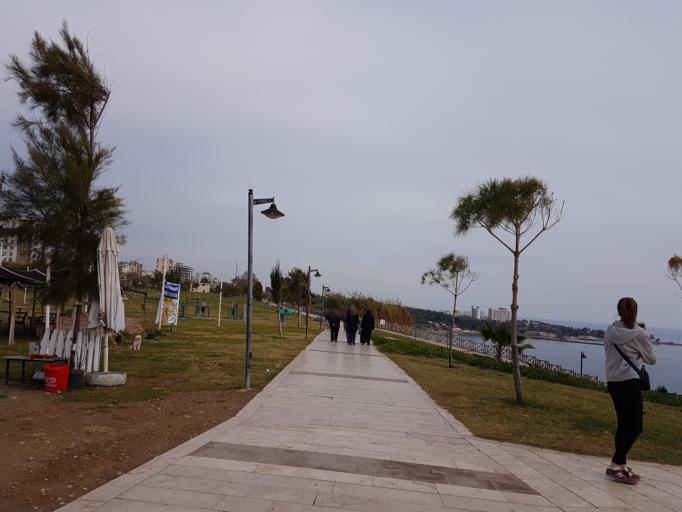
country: TR
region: Antalya
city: Antalya
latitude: 36.8512
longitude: 30.7836
